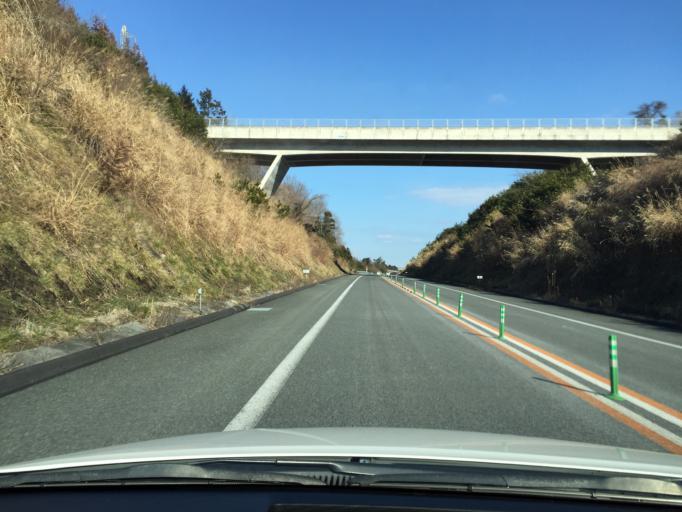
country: JP
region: Fukushima
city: Namie
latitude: 37.3284
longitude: 140.9903
